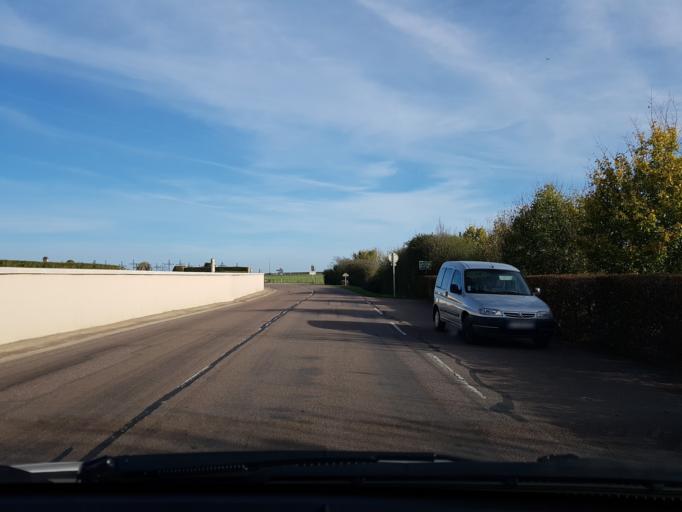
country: FR
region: Bourgogne
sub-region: Departement de la Cote-d'Or
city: Semur-en-Auxois
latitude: 47.5095
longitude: 4.1757
